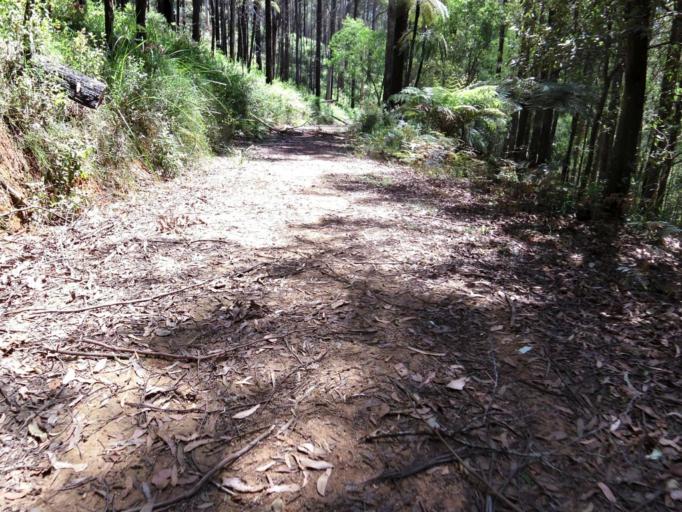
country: AU
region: Victoria
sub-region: Yarra Ranges
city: Millgrove
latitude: -37.8548
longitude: 145.7572
